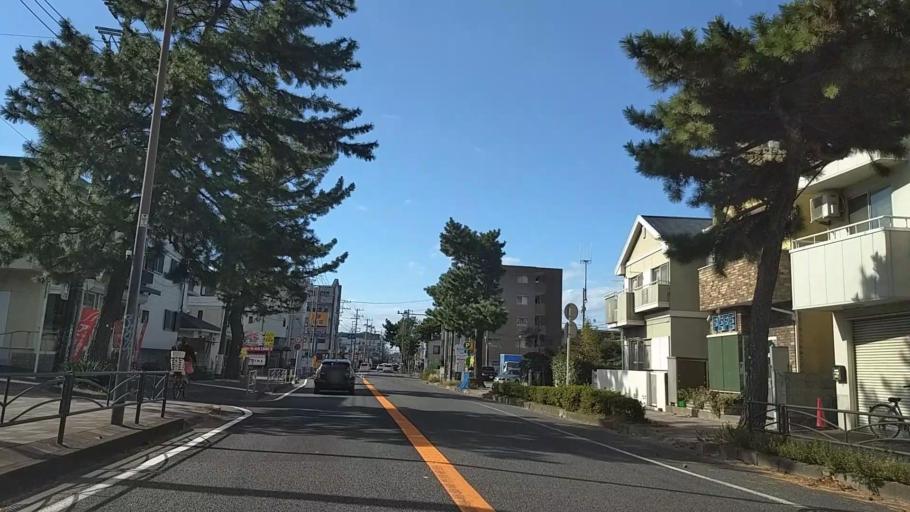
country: JP
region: Kanagawa
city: Fujisawa
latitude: 35.3424
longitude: 139.4391
